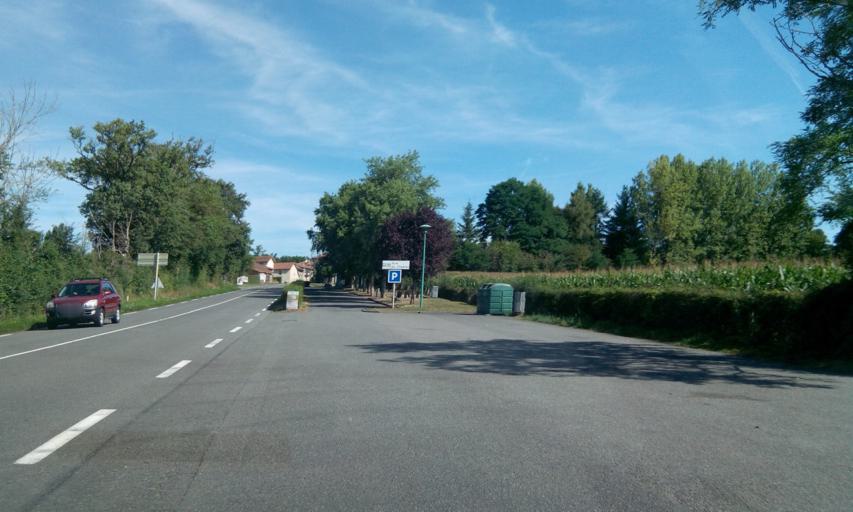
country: FR
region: Poitou-Charentes
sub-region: Departement de la Charente
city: Etagnac
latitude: 45.9294
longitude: 0.7389
